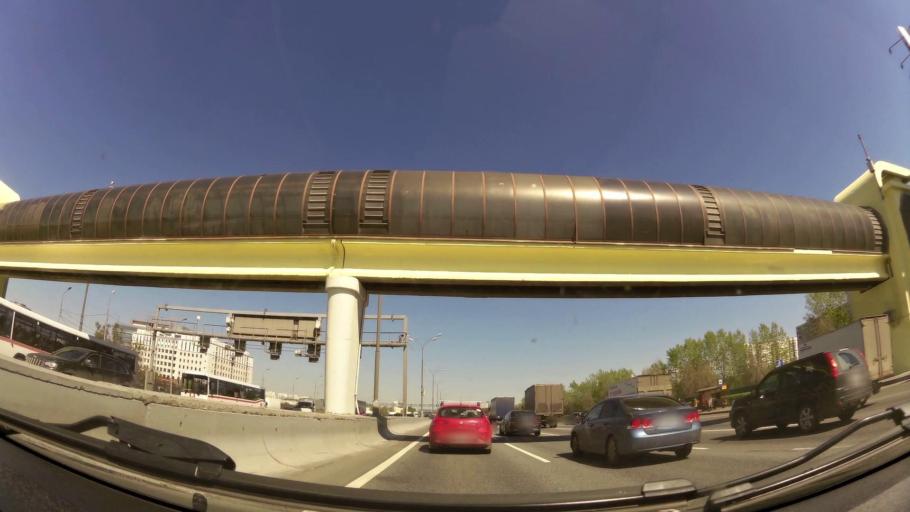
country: RU
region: Moscow
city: Strogino
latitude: 55.8111
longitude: 37.3891
